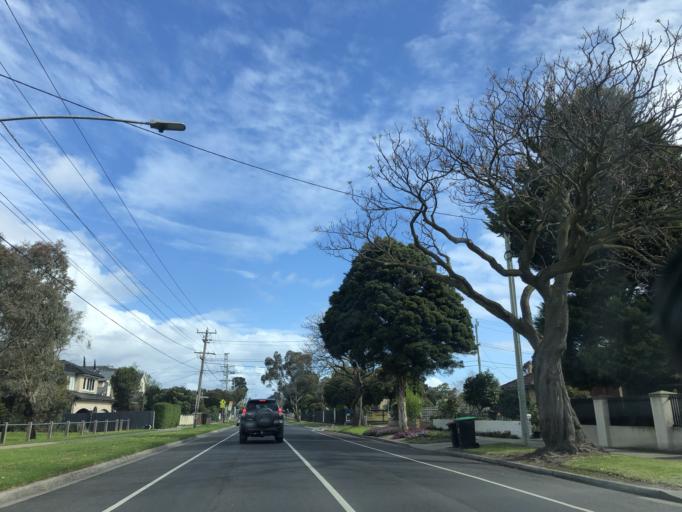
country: AU
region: Victoria
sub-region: Kingston
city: Clayton South
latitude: -37.9340
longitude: 145.1086
